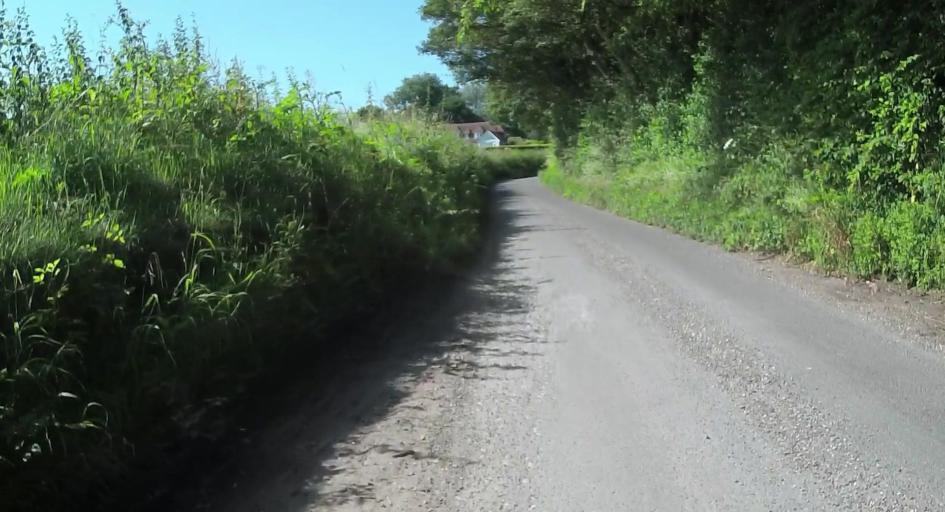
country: GB
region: England
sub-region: Hampshire
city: Kingsley
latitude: 51.1598
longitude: -0.8965
